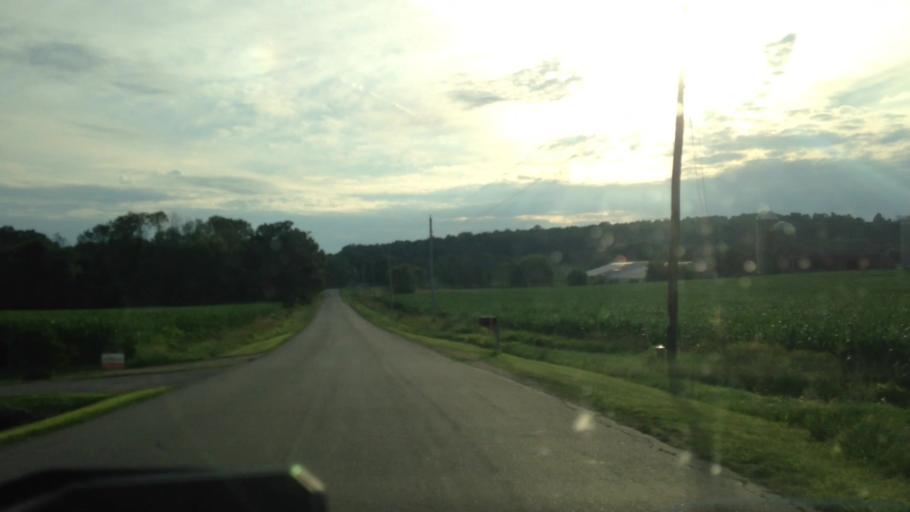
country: US
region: Wisconsin
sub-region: Dodge County
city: Theresa
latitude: 43.4863
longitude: -88.4904
